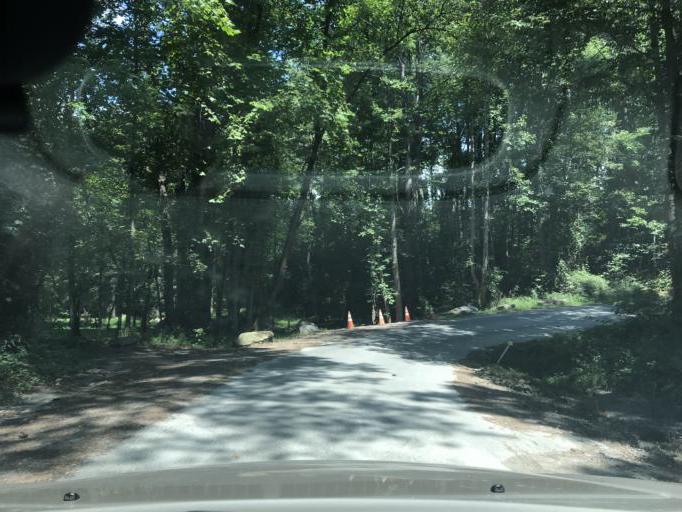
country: US
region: Georgia
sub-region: Dawson County
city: Dawsonville
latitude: 34.3531
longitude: -84.0923
